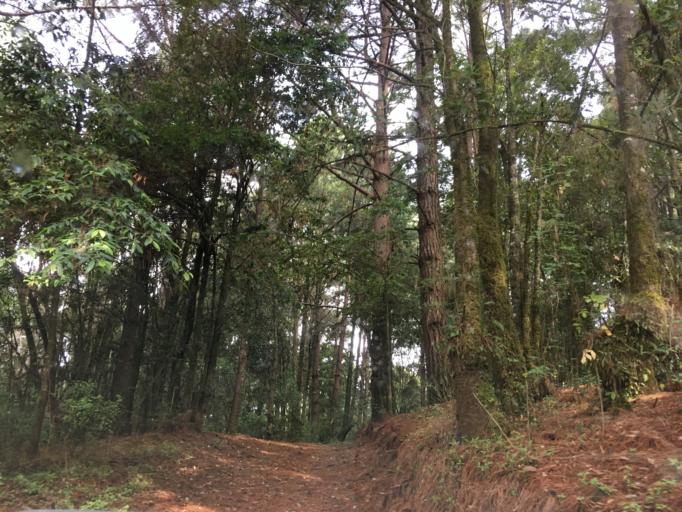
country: MX
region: Michoacan
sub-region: Zitacuaro
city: Francisco Serrato (San Bartolo)
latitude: 19.5192
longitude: -100.3056
